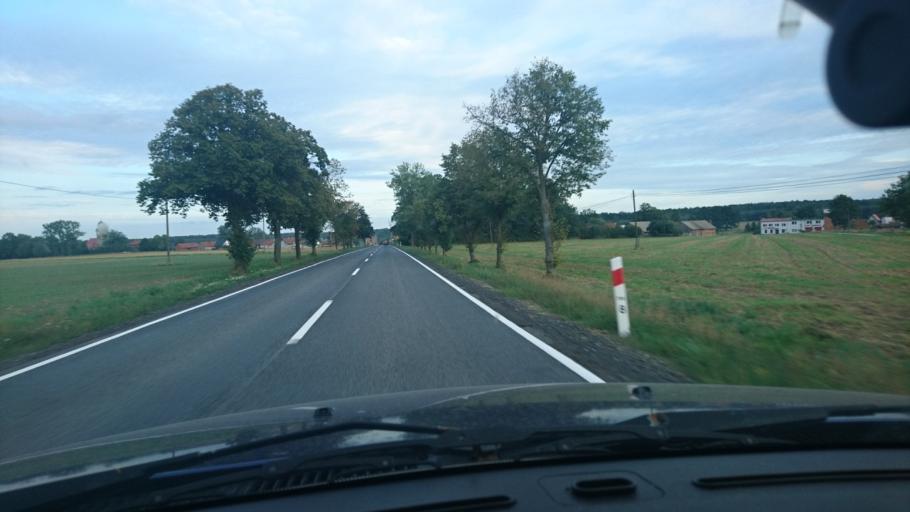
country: PL
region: Silesian Voivodeship
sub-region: Powiat lubliniecki
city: Sierakow Slaski
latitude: 50.8289
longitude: 18.5247
